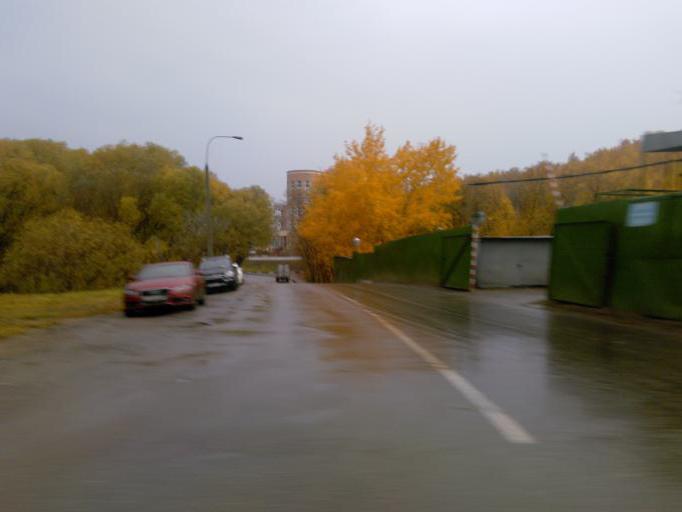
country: RU
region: Moscow
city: Yasenevo
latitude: 55.6057
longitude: 37.5114
